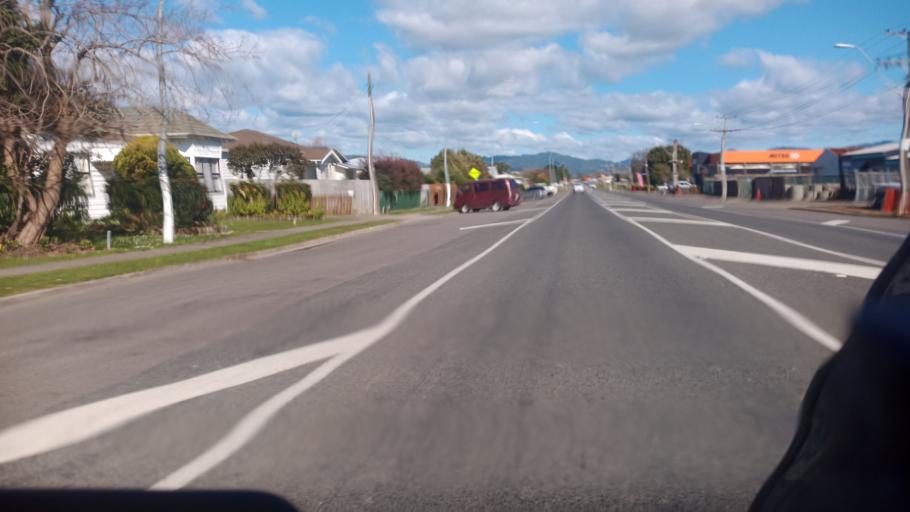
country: NZ
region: Bay of Plenty
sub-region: Opotiki District
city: Opotiki
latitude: -38.0068
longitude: 177.2871
